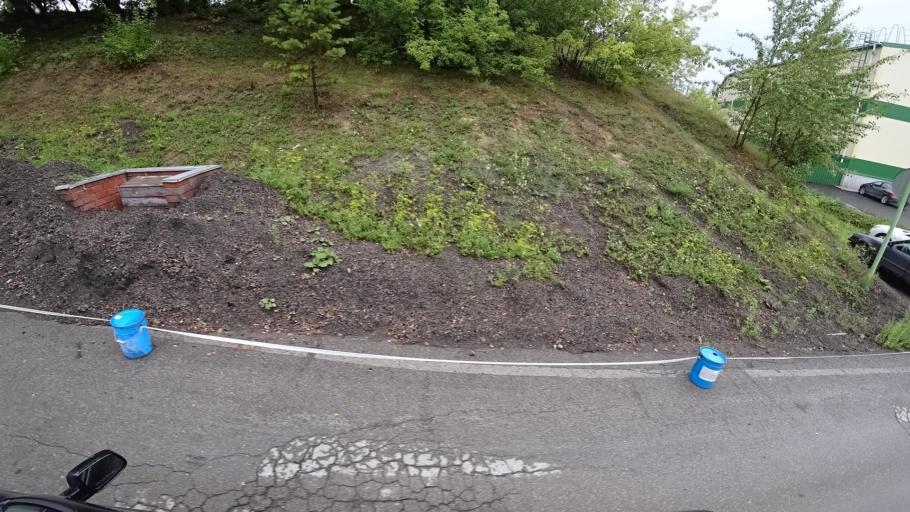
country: RU
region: Sverdlovsk
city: Kamyshlov
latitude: 56.8506
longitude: 62.7088
